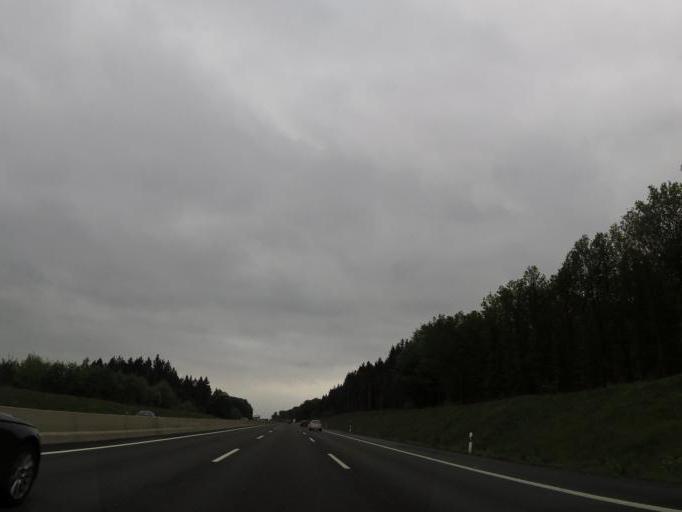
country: DE
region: Lower Saxony
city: Haverlah
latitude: 52.0464
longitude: 10.1834
